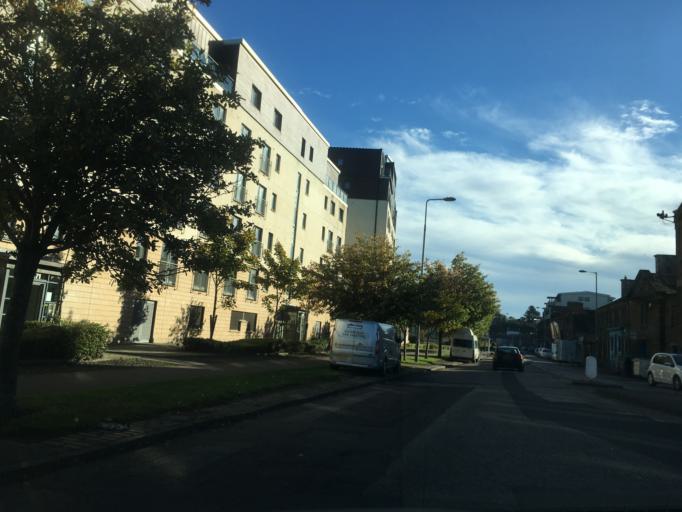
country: GB
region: Scotland
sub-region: Edinburgh
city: Edinburgh
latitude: 55.9810
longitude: -3.2242
